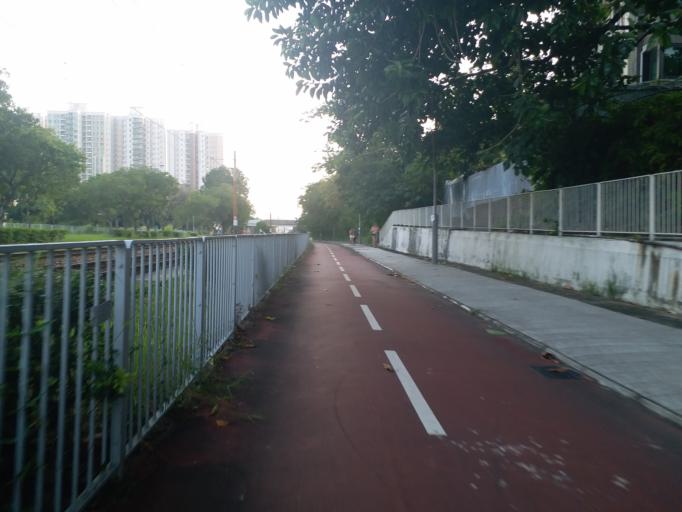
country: HK
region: Yuen Long
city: Yuen Long Kau Hui
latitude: 22.4374
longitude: 114.0027
